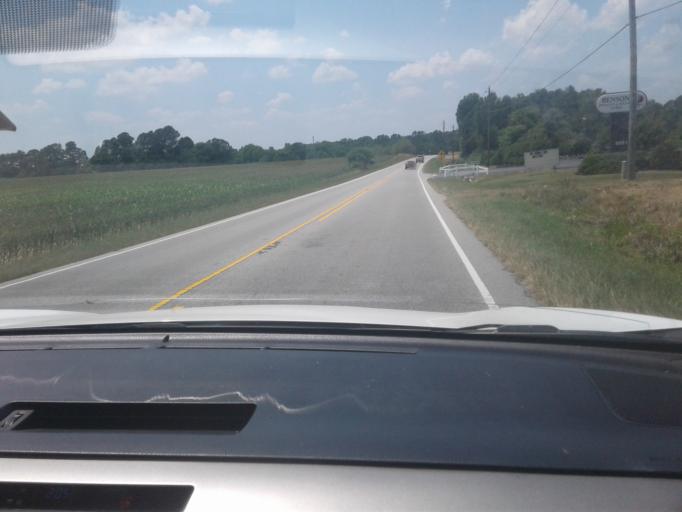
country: US
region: North Carolina
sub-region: Johnston County
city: Benson
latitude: 35.3941
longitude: -78.5925
